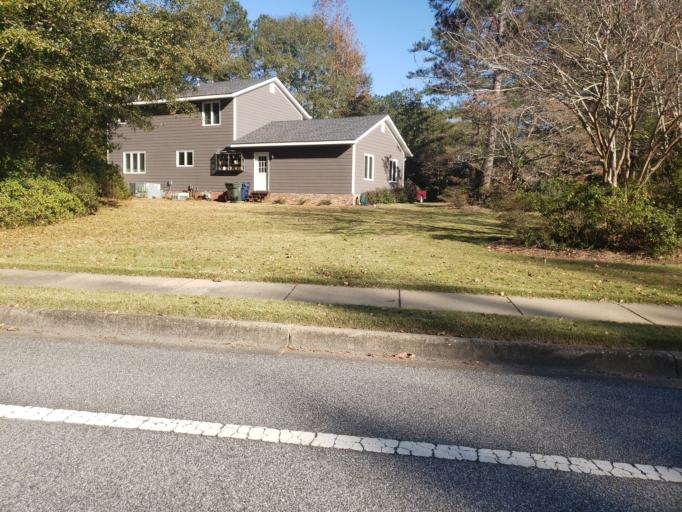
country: US
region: Alabama
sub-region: Lee County
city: Auburn
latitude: 32.5893
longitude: -85.4647
